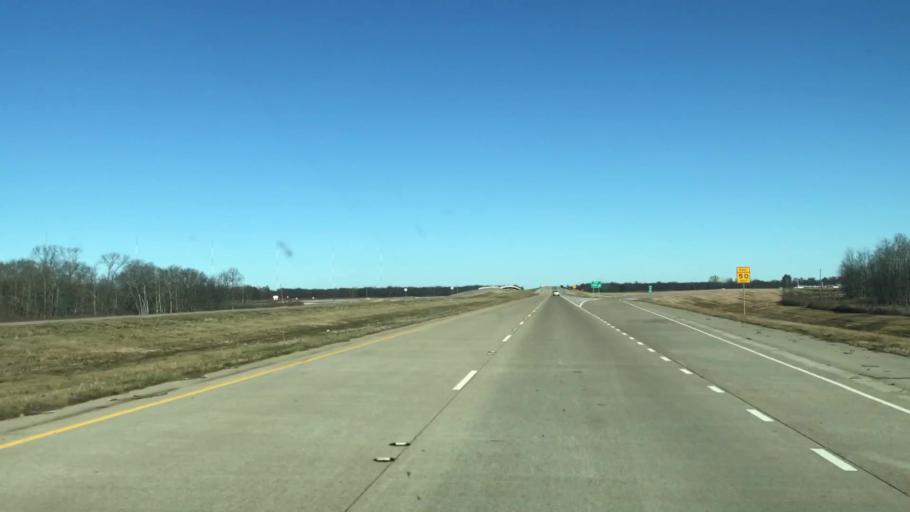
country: US
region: Louisiana
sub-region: Caddo Parish
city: Blanchard
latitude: 32.6696
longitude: -93.8479
